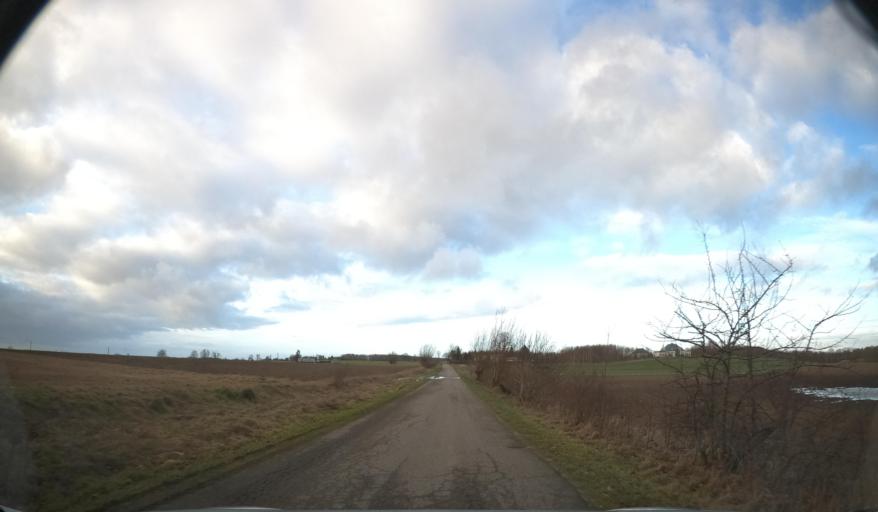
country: PL
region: West Pomeranian Voivodeship
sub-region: Powiat koszalinski
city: Mielno
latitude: 54.1676
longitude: 16.0357
